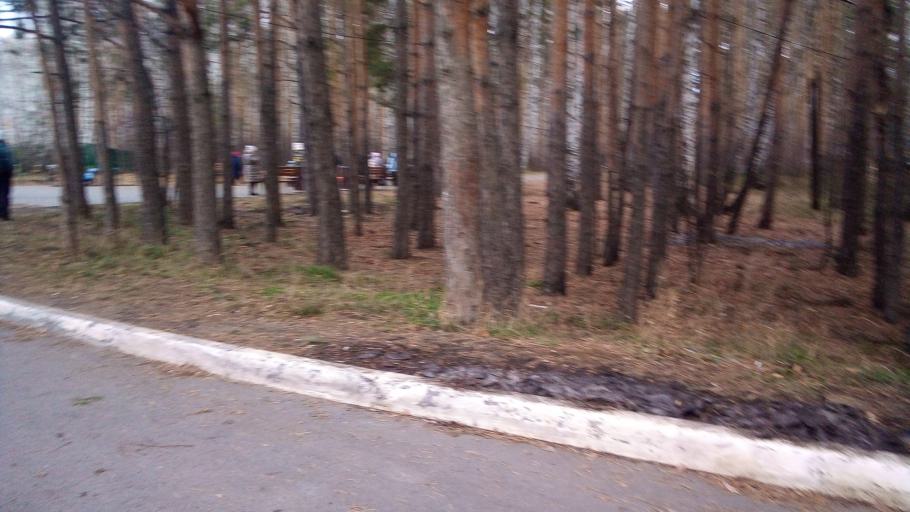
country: RU
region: Chelyabinsk
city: Roshchino
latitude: 55.1941
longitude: 61.2863
